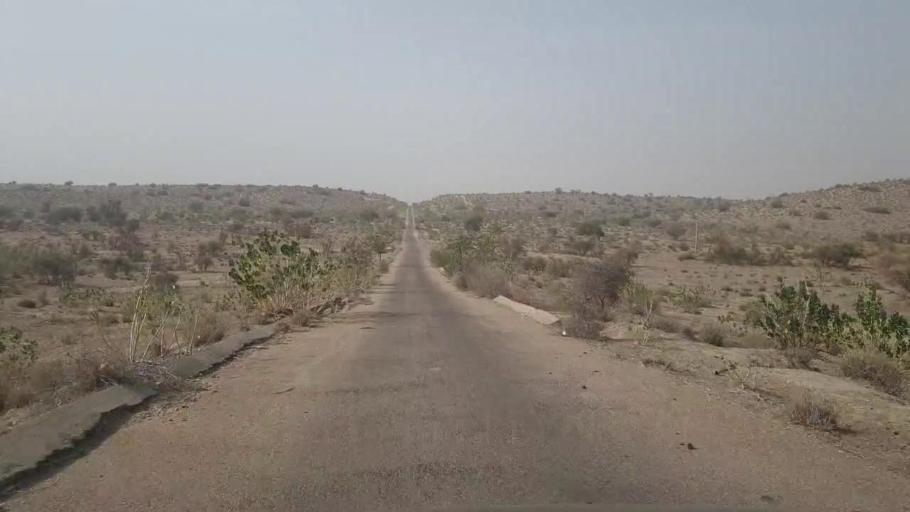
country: PK
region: Sindh
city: Chor
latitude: 25.6077
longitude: 69.9354
